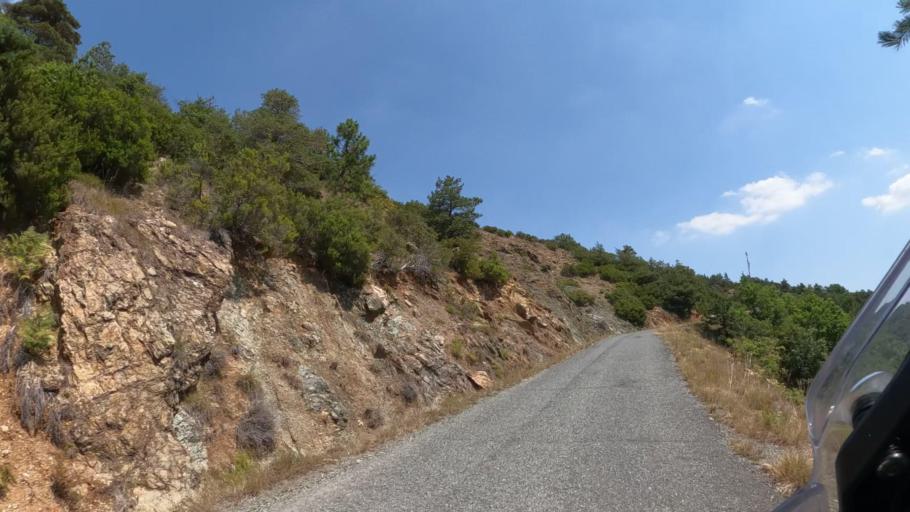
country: IT
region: Piedmont
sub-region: Provincia di Alessandria
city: Ponzone
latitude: 44.5427
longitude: 8.4726
